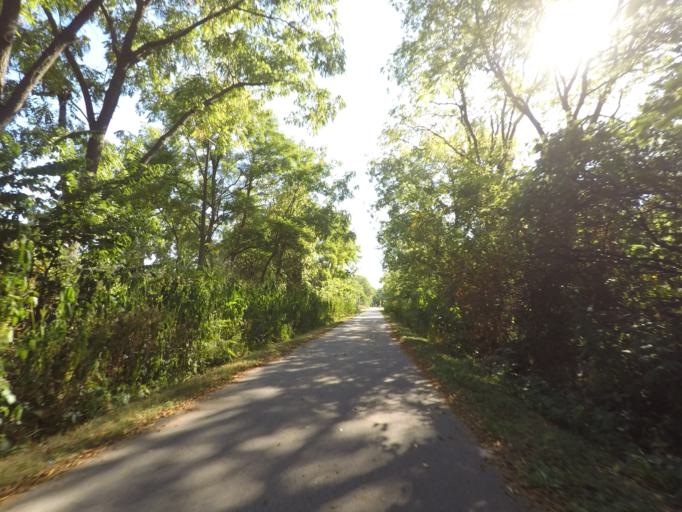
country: US
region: Wisconsin
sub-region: Waukesha County
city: Waukesha
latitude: 43.0077
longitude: -88.2180
